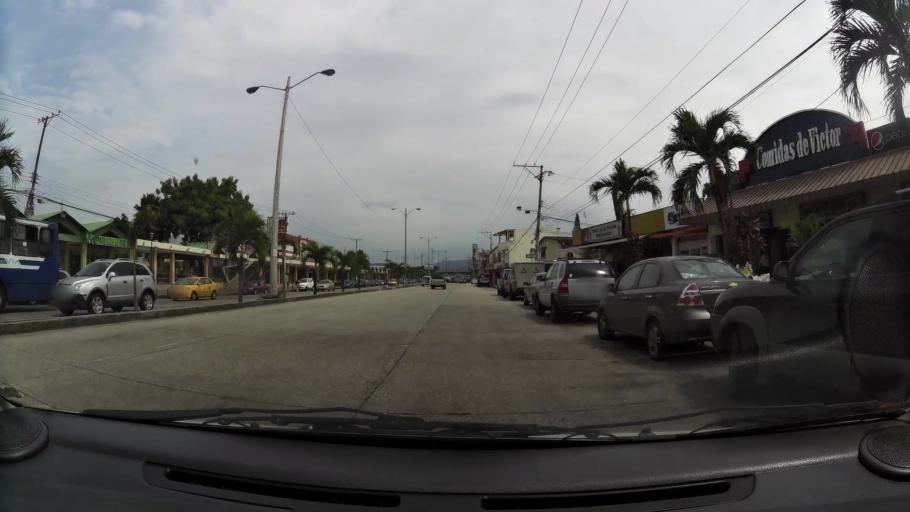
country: EC
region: Guayas
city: Eloy Alfaro
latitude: -2.1435
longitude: -79.8929
